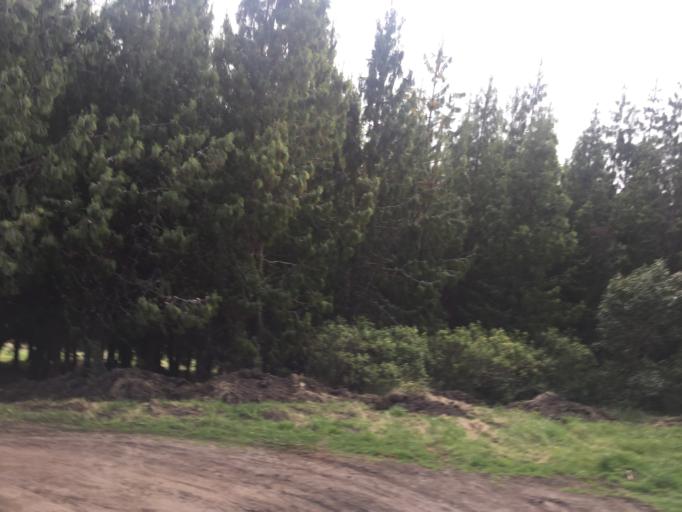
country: EC
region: Imbabura
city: Ibarra
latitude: 0.2251
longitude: -78.1245
